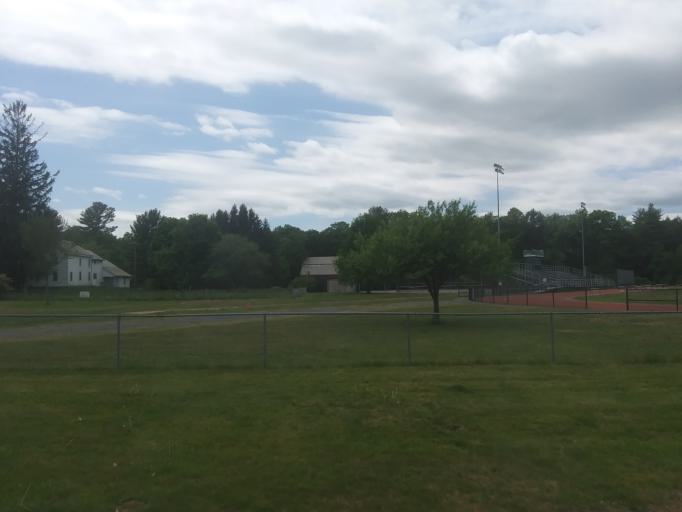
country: US
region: Massachusetts
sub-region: Franklin County
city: Shelburne Falls
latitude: 42.6151
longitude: -72.7568
